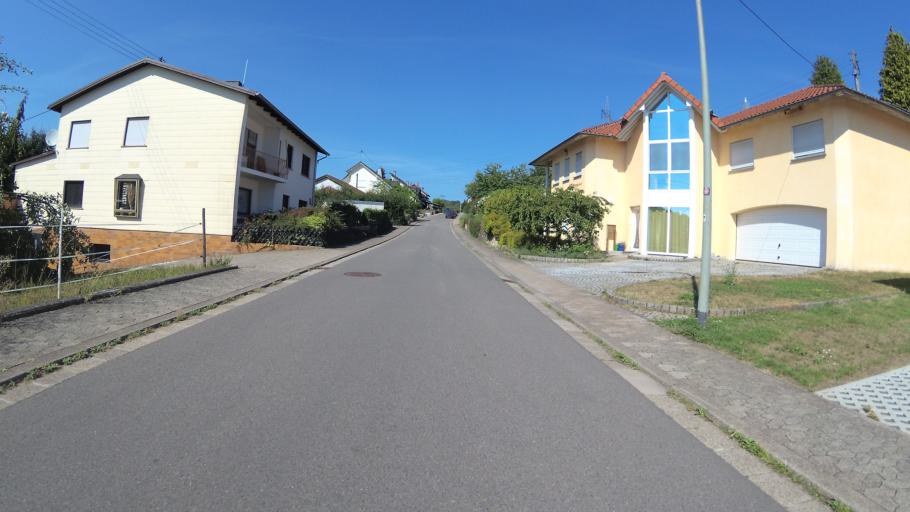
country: DE
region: Saarland
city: Eppelborn
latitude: 49.3746
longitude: 6.9868
